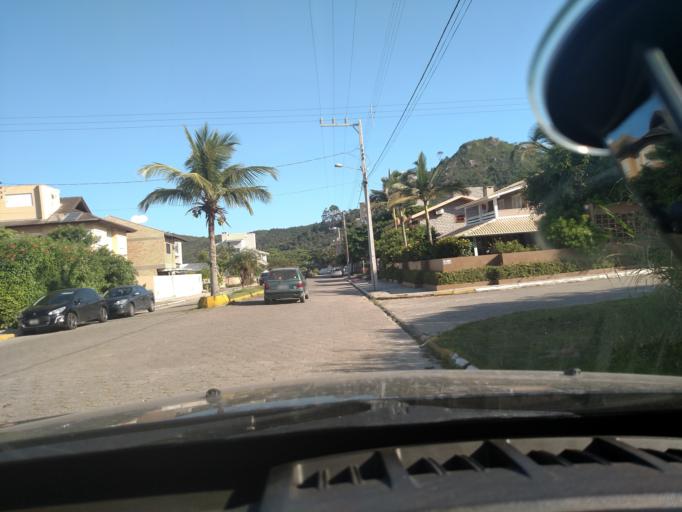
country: BR
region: Santa Catarina
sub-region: Porto Belo
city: Porto Belo
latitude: -27.1952
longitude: -48.4977
